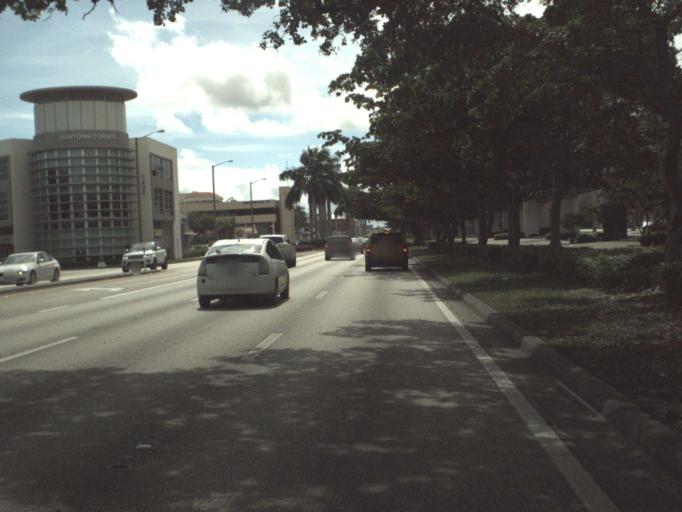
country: US
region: Florida
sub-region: Miami-Dade County
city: South Miami
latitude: 25.7112
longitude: -80.2812
